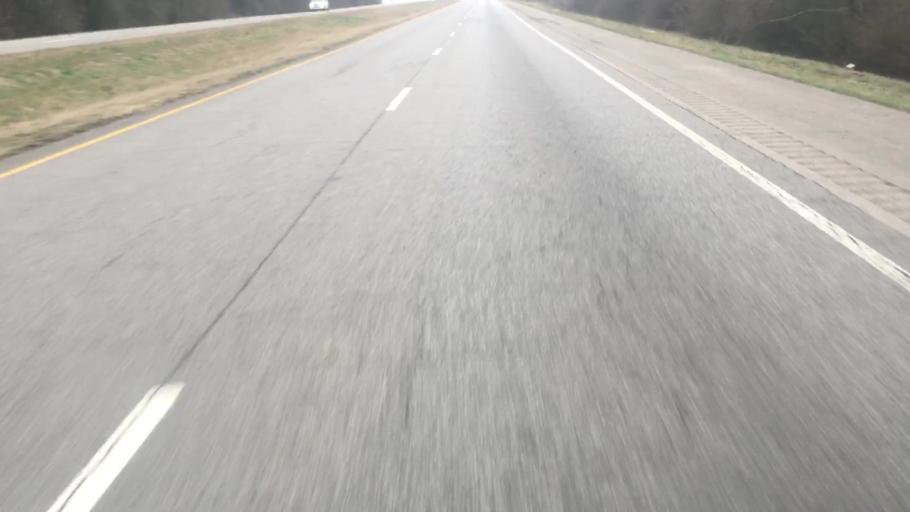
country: US
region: Alabama
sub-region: Jefferson County
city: Graysville
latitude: 33.6536
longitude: -86.9741
